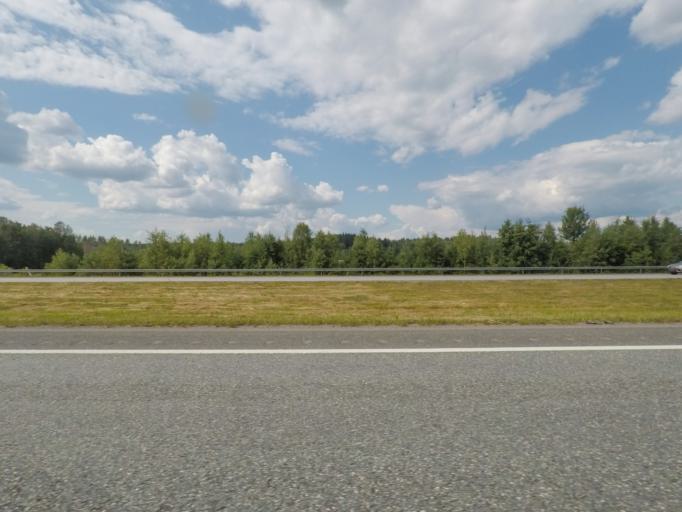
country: FI
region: Paijanne Tavastia
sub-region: Lahti
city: Nastola
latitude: 61.0731
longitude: 25.8848
